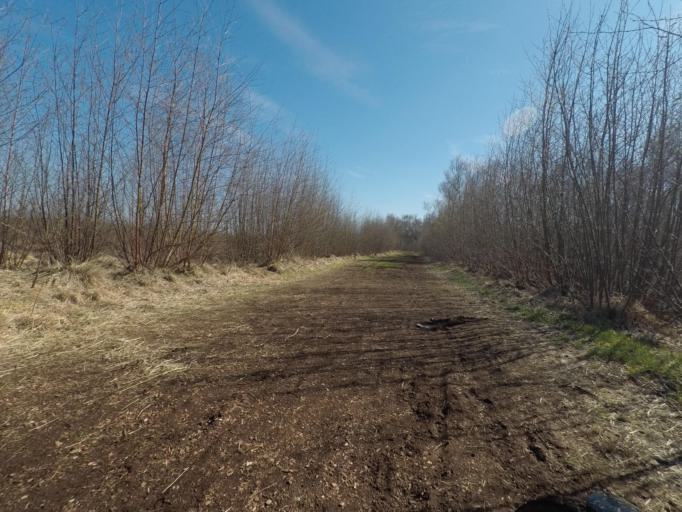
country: DE
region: Hamburg
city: Langenhorn
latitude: 53.6531
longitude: 9.9727
